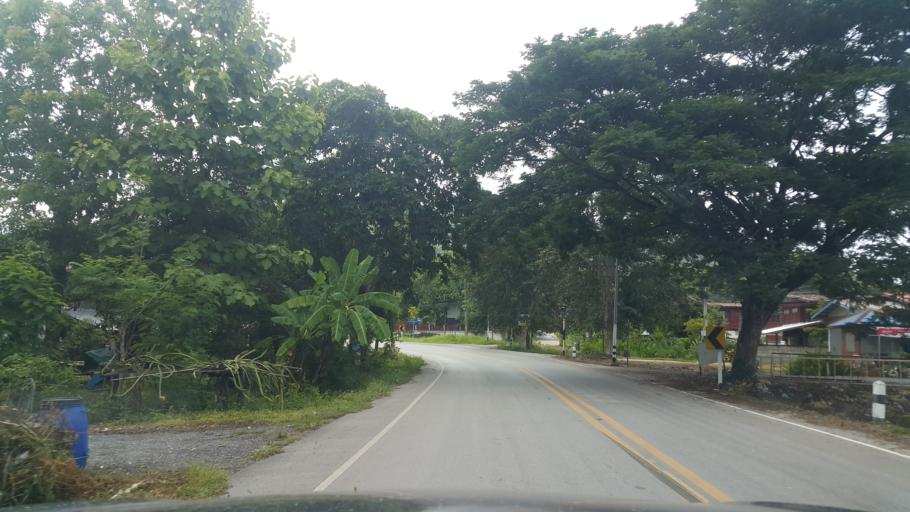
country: TH
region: Uttaradit
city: Thong Saen Khan
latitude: 17.4098
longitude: 100.3226
